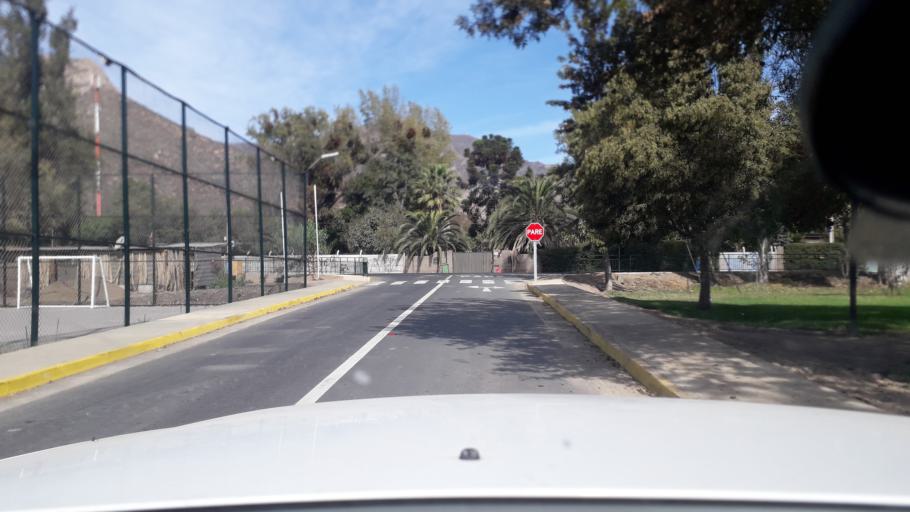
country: CL
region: Valparaiso
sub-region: Provincia de San Felipe
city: Llaillay
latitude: -32.8029
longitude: -70.9049
